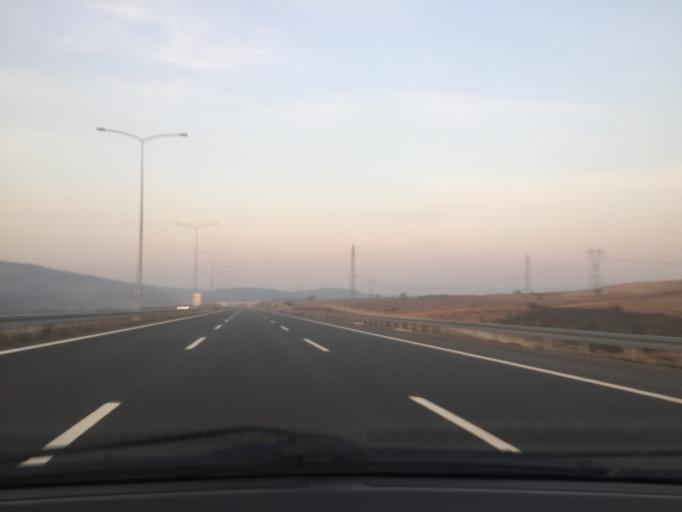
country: TR
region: Bursa
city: Mahmudiye
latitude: 40.2738
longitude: 28.5908
